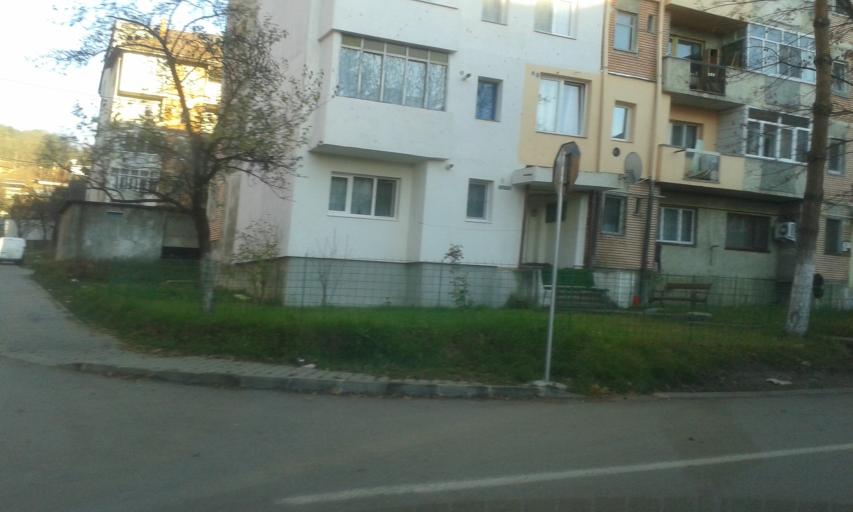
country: RO
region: Hunedoara
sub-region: Municipiul Petrosani
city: Petrosani
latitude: 45.4167
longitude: 23.3749
